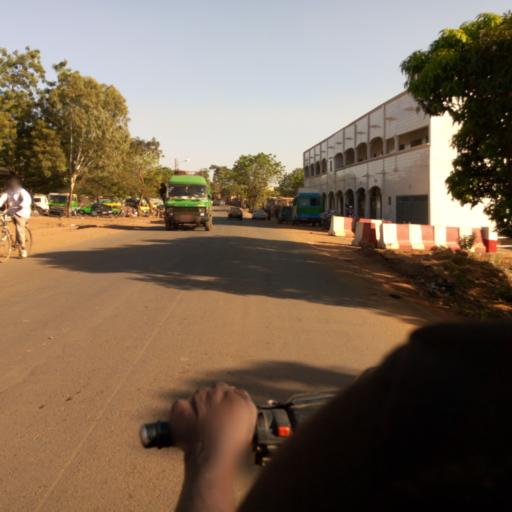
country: ML
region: Bamako
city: Bamako
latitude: 12.6587
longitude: -8.0319
